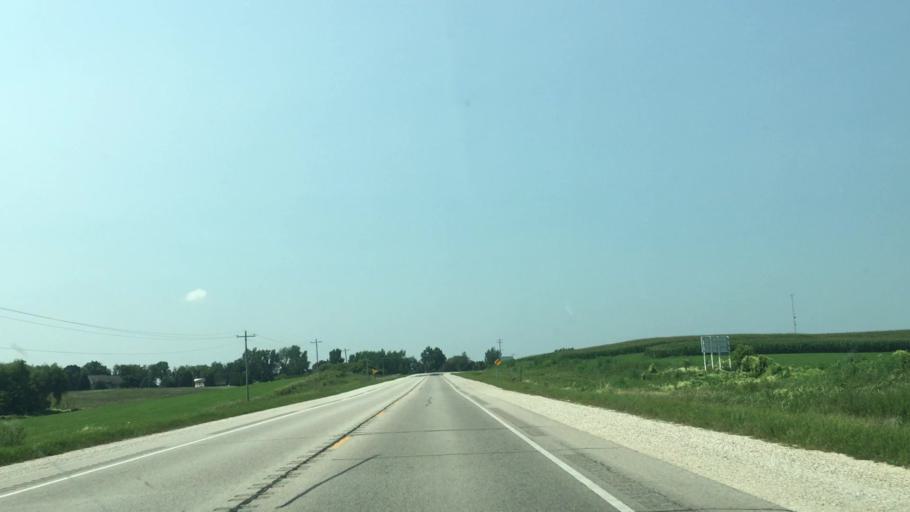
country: US
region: Iowa
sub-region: Winneshiek County
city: Decorah
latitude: 43.1918
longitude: -91.8685
